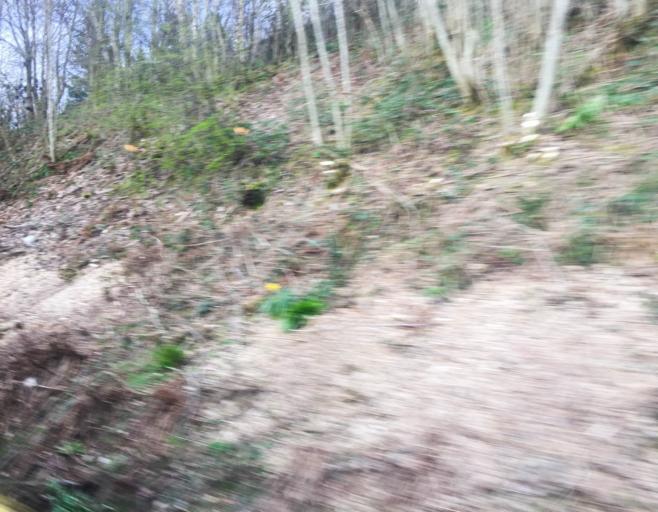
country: GB
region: Scotland
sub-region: West Dunbartonshire
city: Old Kilpatrick
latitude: 55.9220
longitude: -4.4495
